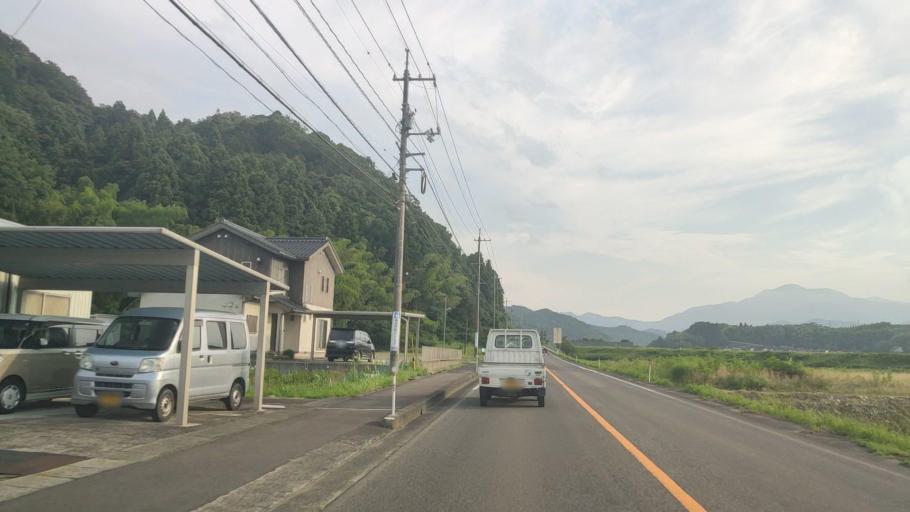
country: JP
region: Tottori
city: Kurayoshi
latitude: 35.3839
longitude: 133.7787
